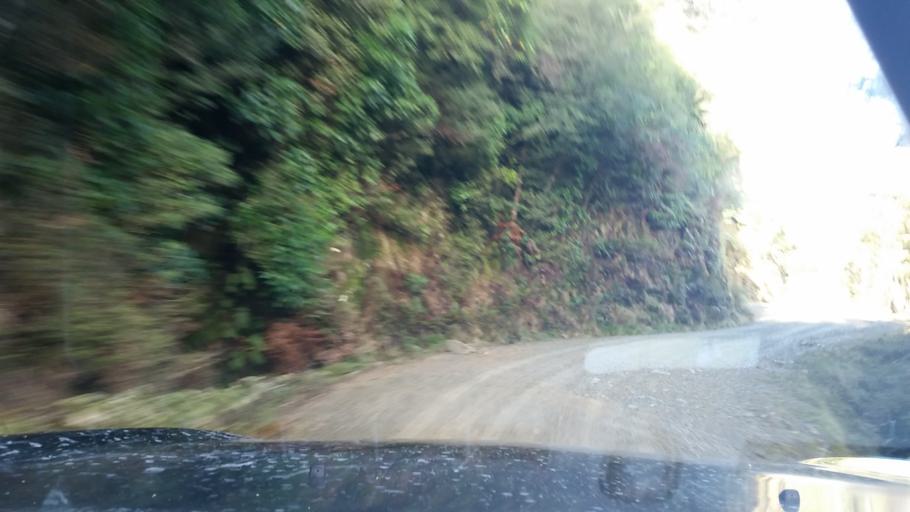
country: NZ
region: Marlborough
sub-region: Marlborough District
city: Picton
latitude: -41.0842
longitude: 174.1489
